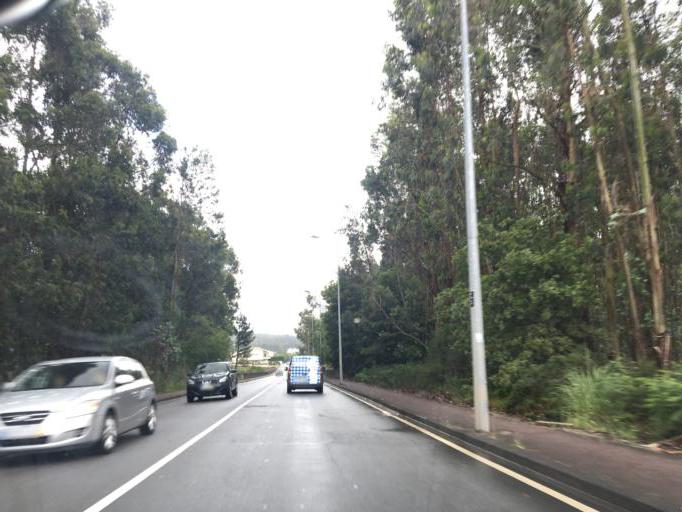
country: PT
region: Porto
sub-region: Maia
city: Nogueira
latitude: 41.2557
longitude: -8.5955
